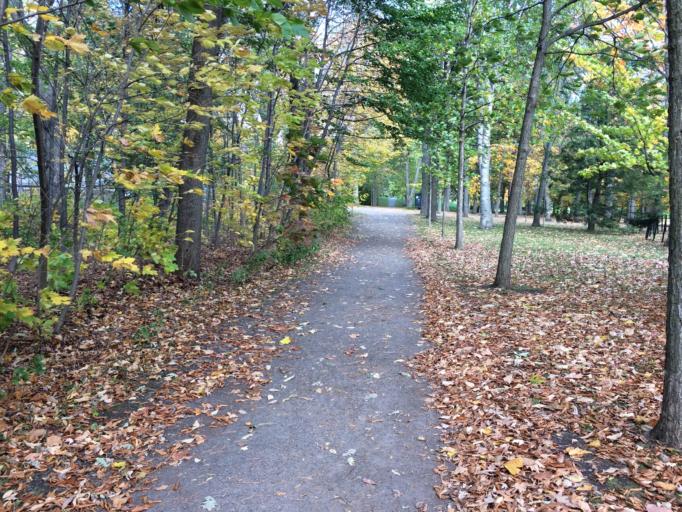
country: CA
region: Quebec
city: Quebec
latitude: 46.7865
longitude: -71.2395
